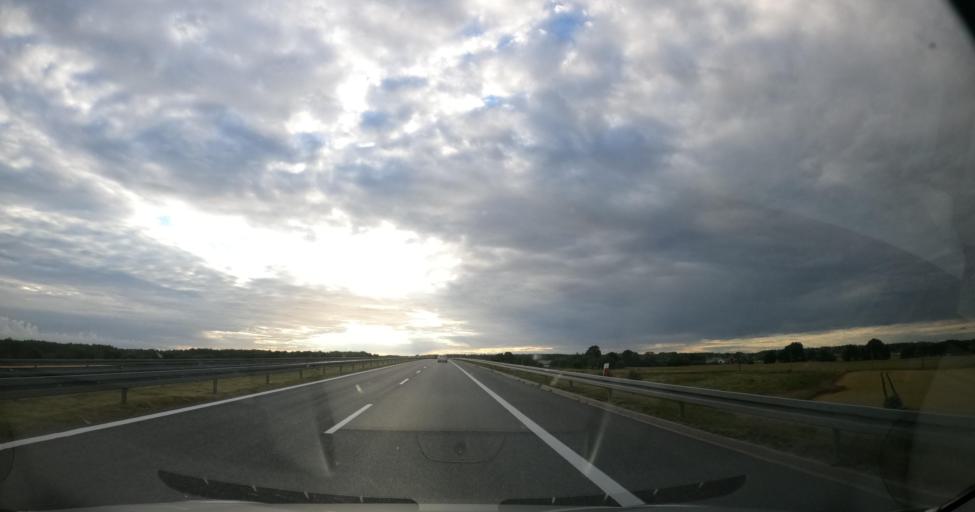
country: PL
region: Pomeranian Voivodeship
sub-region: Powiat slupski
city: Kobylnica
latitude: 54.4369
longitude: 16.9586
